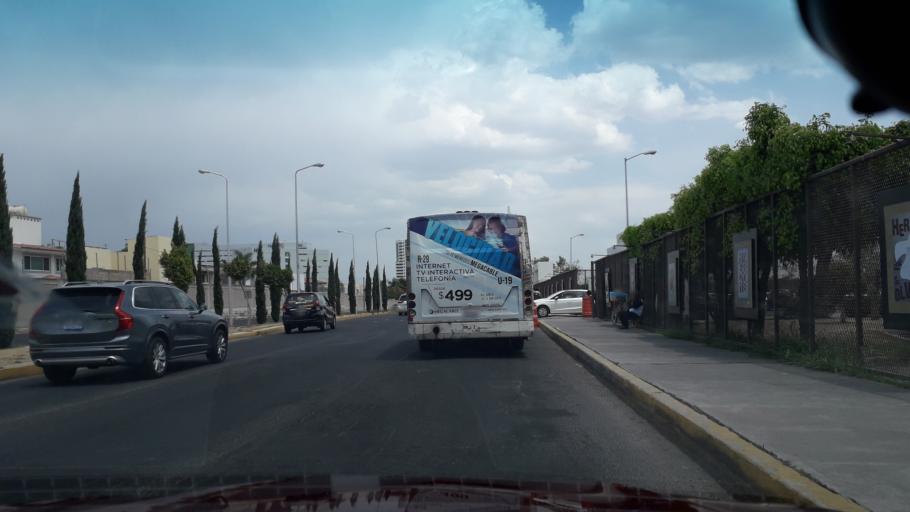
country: MX
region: Puebla
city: Tlazcalancingo
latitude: 19.0218
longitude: -98.2407
